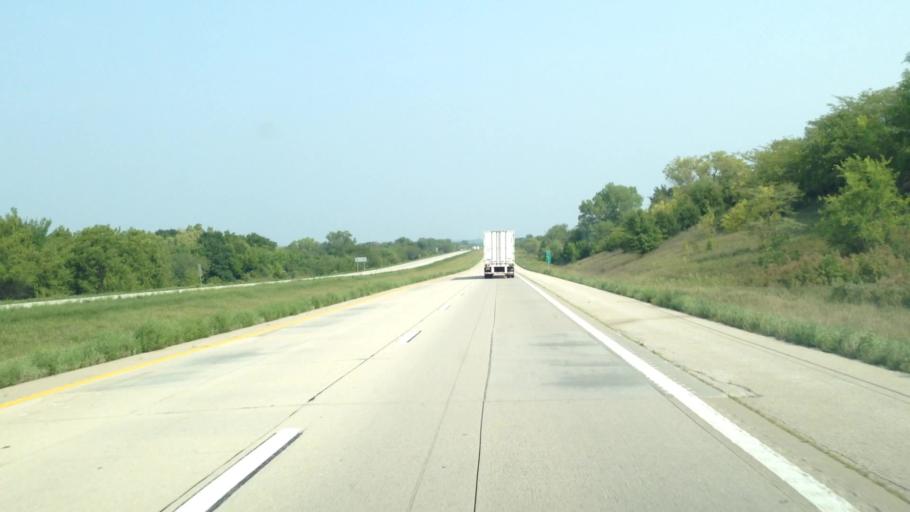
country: US
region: Missouri
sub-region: Daviess County
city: Gallatin
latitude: 39.9825
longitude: -94.0944
